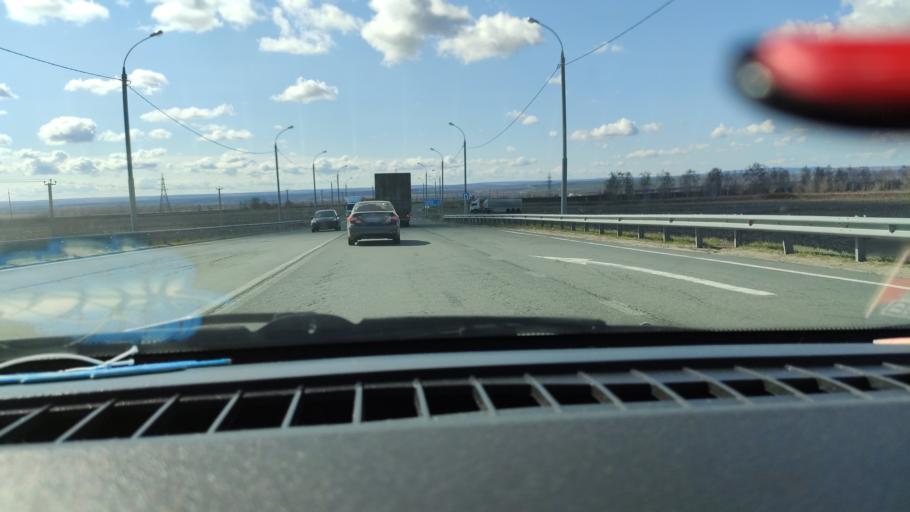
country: RU
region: Samara
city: Varlamovo
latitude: 53.1872
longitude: 48.2912
